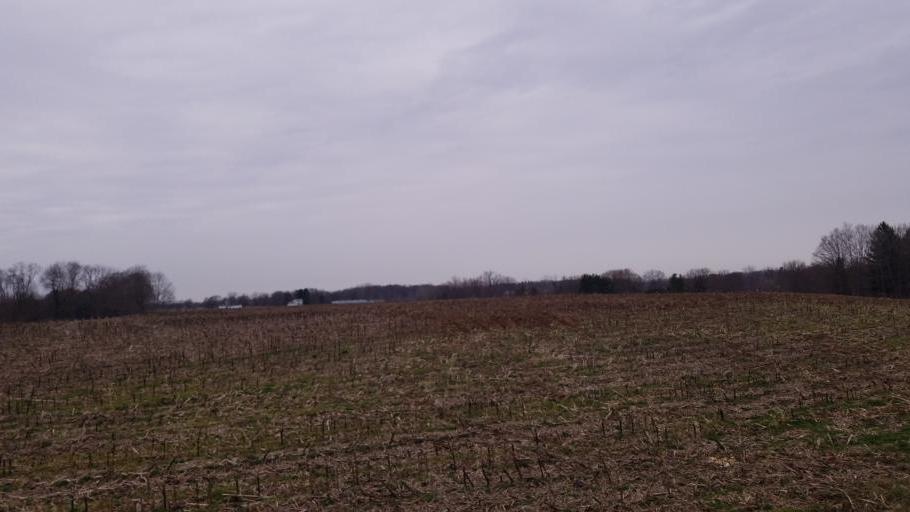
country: US
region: Ohio
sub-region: Knox County
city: Fredericktown
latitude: 40.5077
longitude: -82.5057
